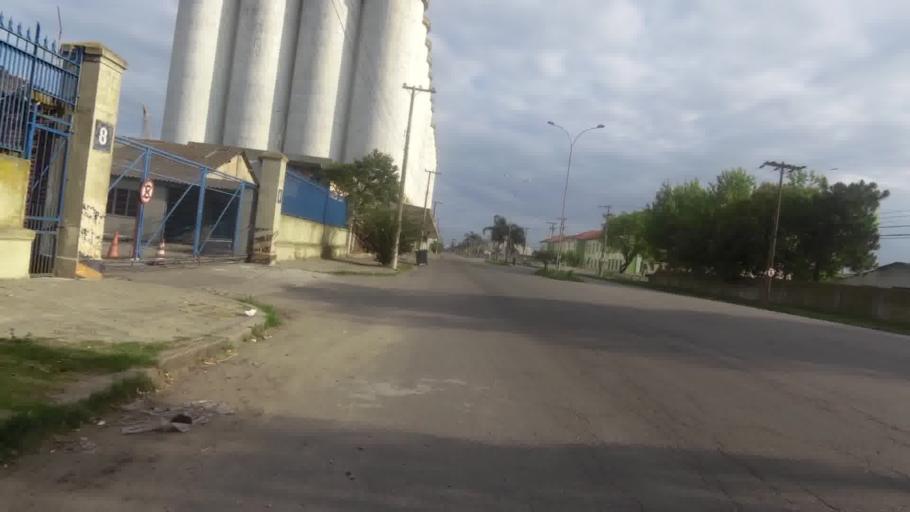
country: BR
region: Rio Grande do Sul
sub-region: Rio Grande
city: Rio Grande
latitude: -32.0341
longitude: -52.0793
